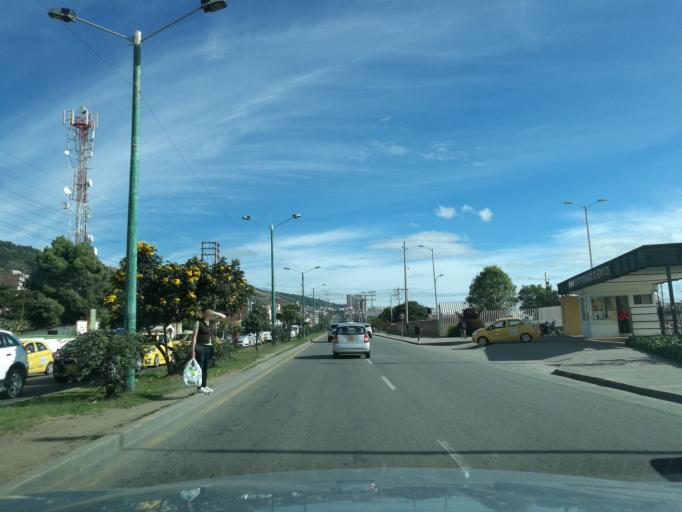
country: CO
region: Boyaca
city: Tunja
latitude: 5.5574
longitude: -73.3499
